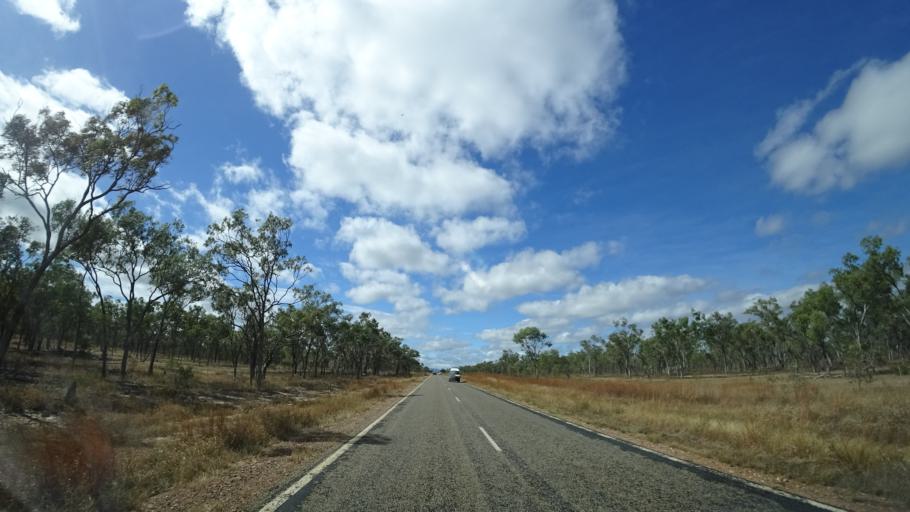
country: AU
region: Queensland
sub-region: Cairns
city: Port Douglas
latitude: -16.4893
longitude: 144.9213
